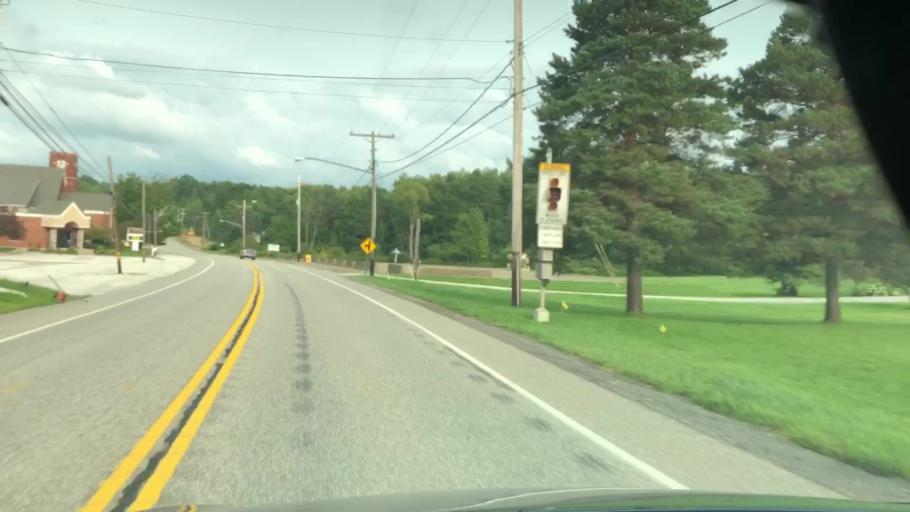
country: US
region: Pennsylvania
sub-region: Erie County
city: Wesleyville
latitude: 42.0662
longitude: -79.9719
